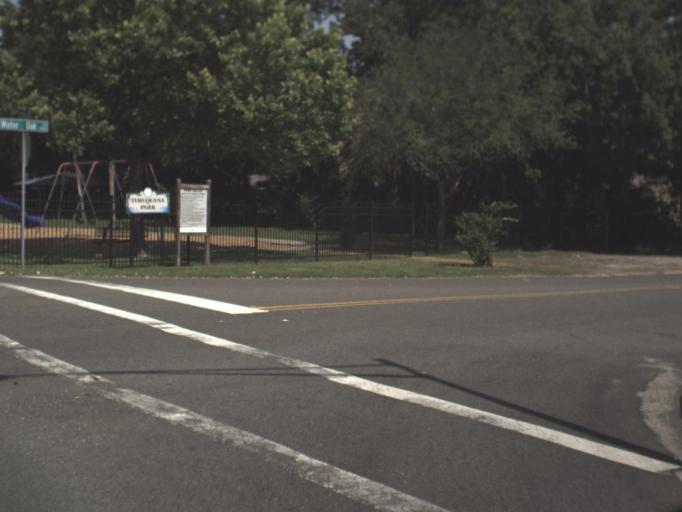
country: US
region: Florida
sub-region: Clay County
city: Orange Park
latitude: 30.2477
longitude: -81.6984
